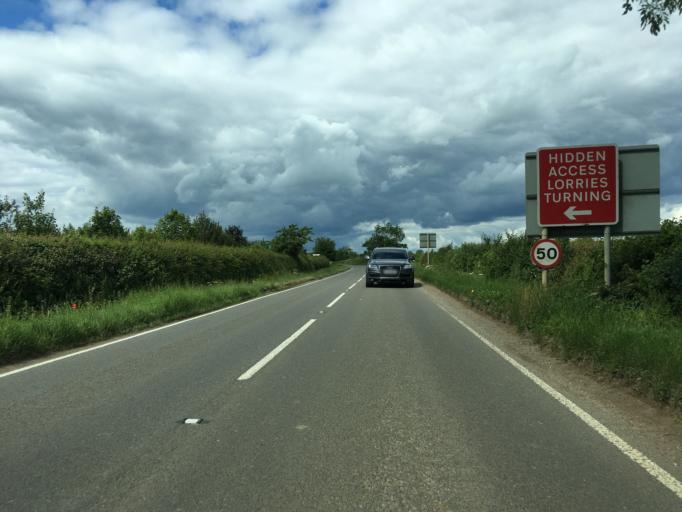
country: GB
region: England
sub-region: Northamptonshire
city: Brackley
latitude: 52.0792
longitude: -1.1482
